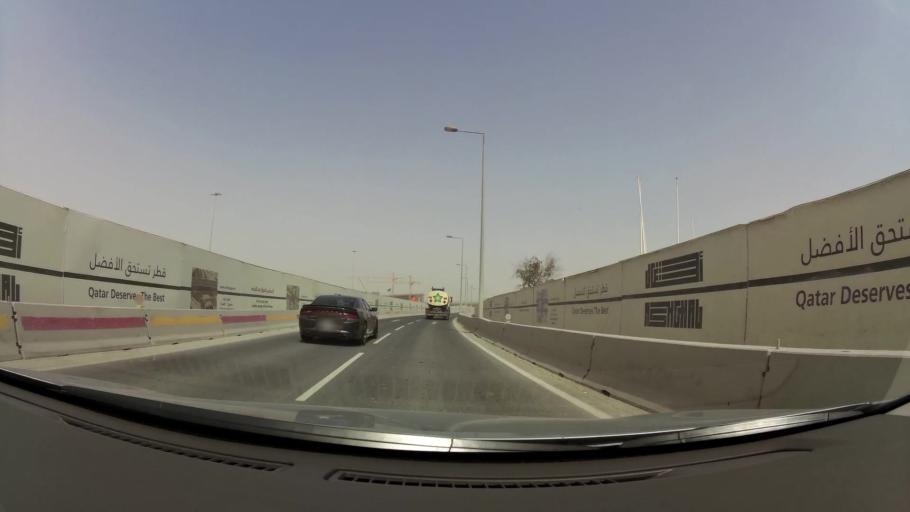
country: QA
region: Baladiyat ad Dawhah
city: Doha
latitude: 25.2910
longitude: 51.4780
